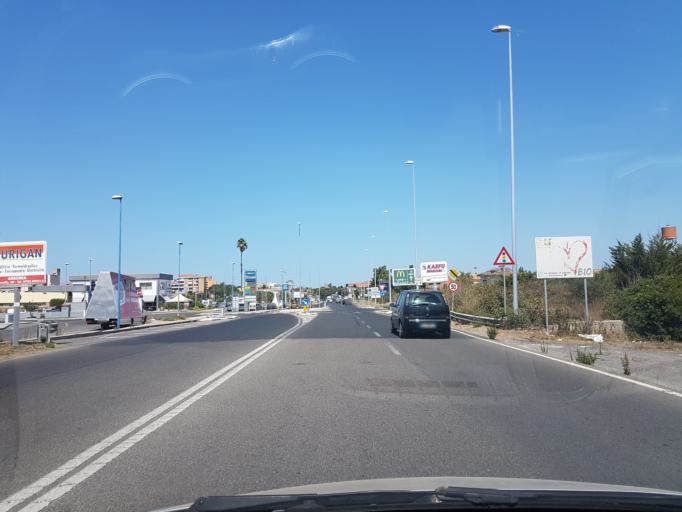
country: IT
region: Sardinia
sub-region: Provincia di Oristano
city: Oristano
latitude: 39.8900
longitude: 8.6003
